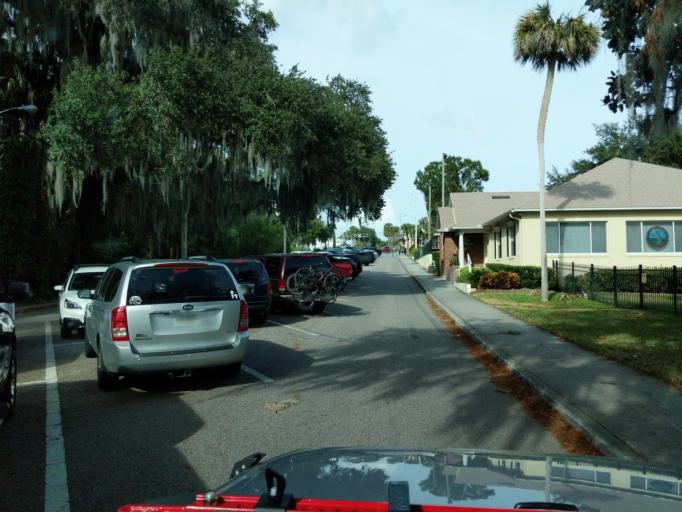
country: US
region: Florida
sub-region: Lake County
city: Mount Dora
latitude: 28.7967
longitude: -81.6447
